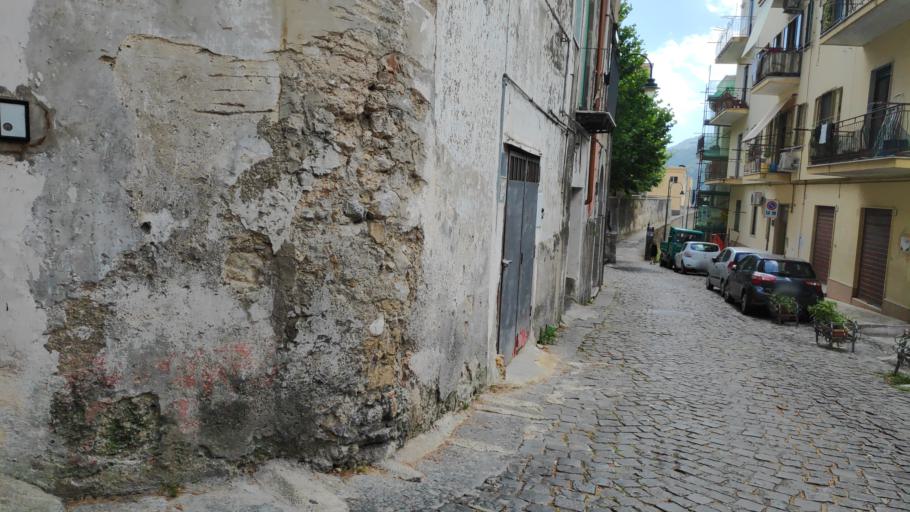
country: IT
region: Campania
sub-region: Provincia di Salerno
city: Vietri sul Mare
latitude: 40.6703
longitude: 14.7271
